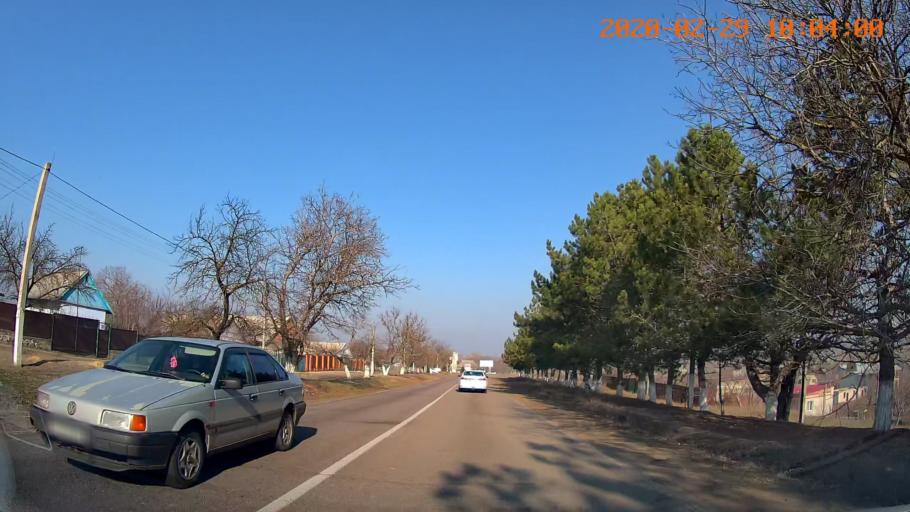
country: MD
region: Causeni
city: Chitcani
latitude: 46.7947
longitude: 29.6778
